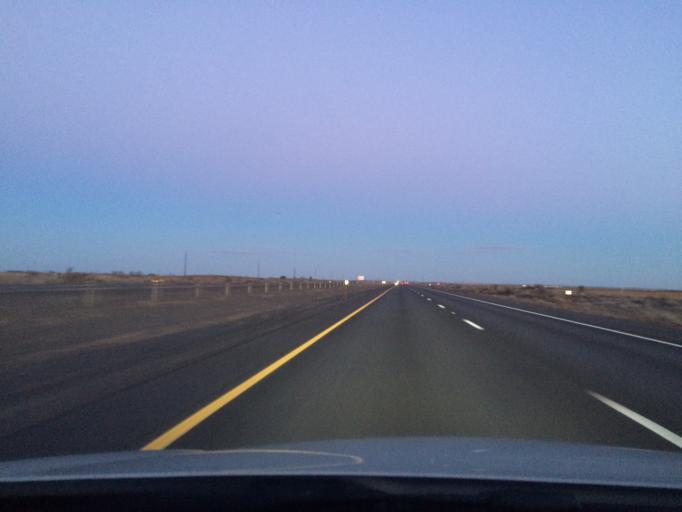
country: US
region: Washington
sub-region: Grant County
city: Royal City
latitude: 47.1039
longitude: -119.6052
